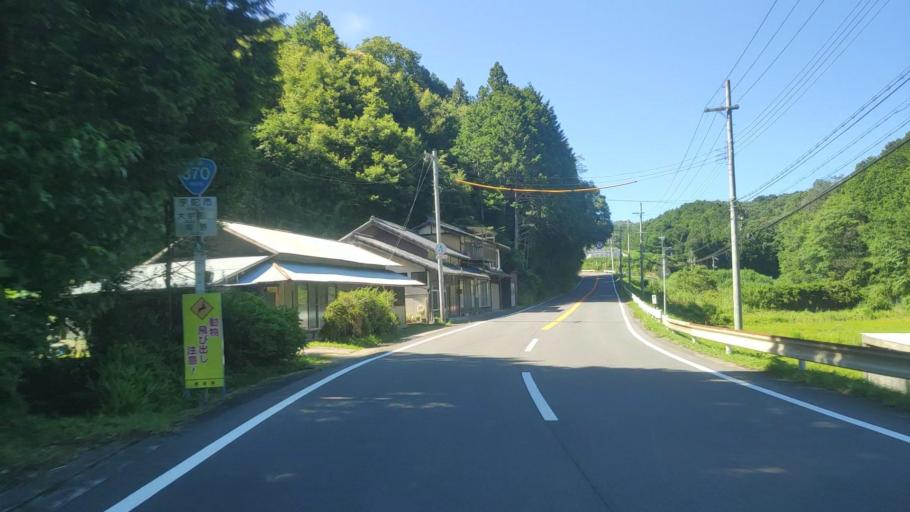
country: JP
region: Nara
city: Haibara-akanedai
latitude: 34.4543
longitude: 135.9362
